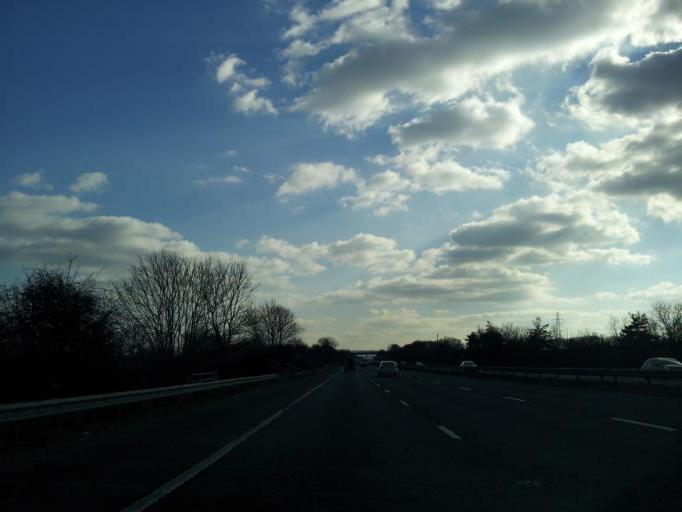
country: GB
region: England
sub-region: Somerset
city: North Petherton
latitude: 51.0604
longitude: -3.0211
